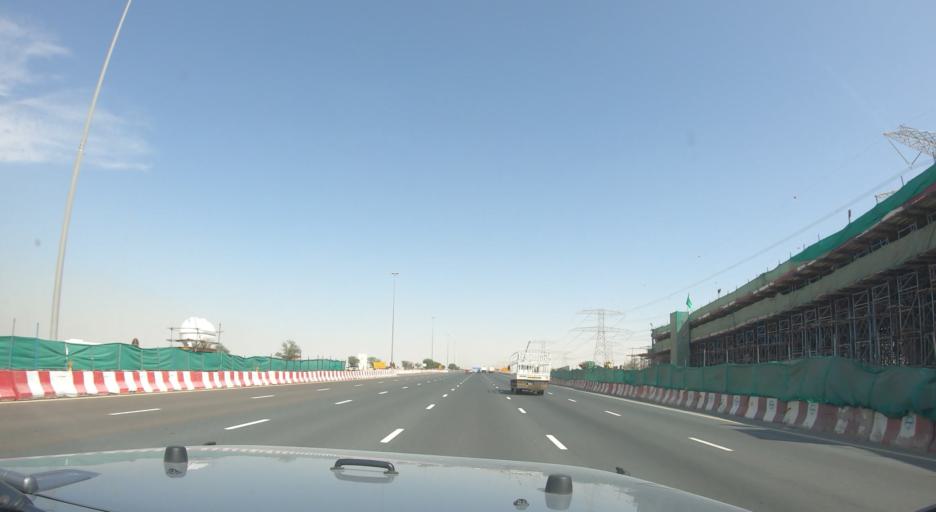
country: AE
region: Ash Shariqah
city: Sharjah
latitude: 25.1781
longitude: 55.5158
